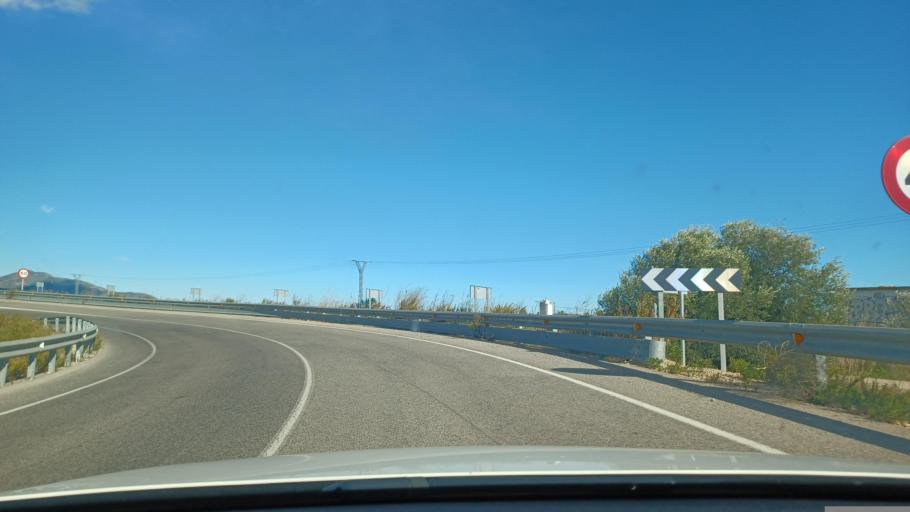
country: ES
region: Valencia
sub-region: Provincia de Castello
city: Vinaros
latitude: 40.4973
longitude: 0.4658
